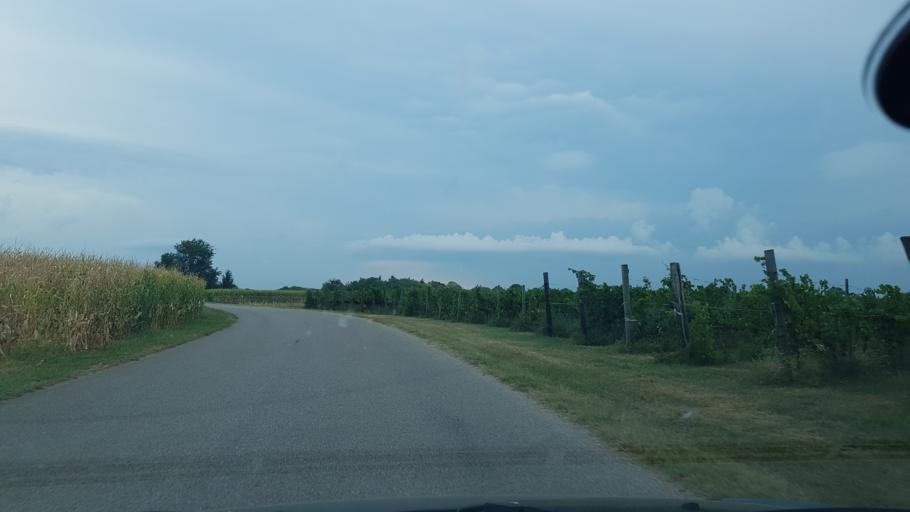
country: IT
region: Friuli Venezia Giulia
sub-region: Provincia di Gorizia
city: Farra d'Isonzo
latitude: 45.9105
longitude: 13.5061
